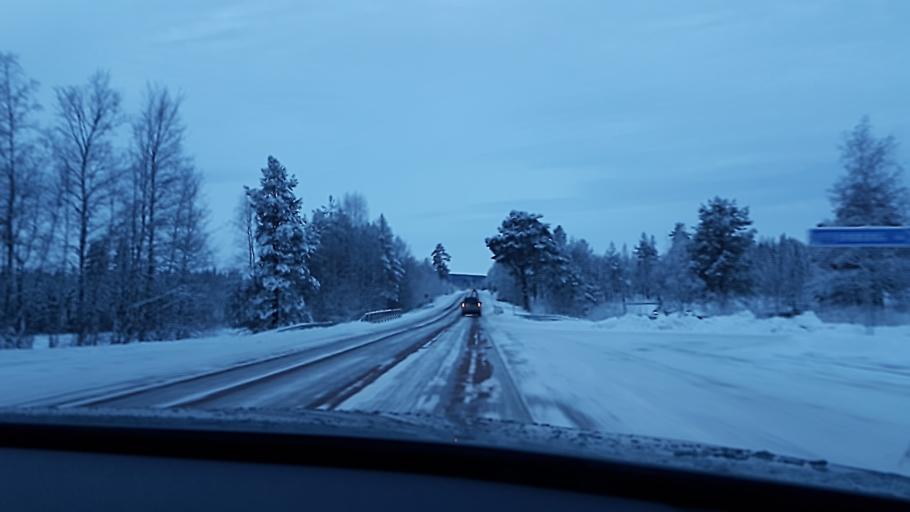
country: SE
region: Jaemtland
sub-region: Harjedalens Kommun
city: Sveg
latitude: 62.0452
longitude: 14.4751
